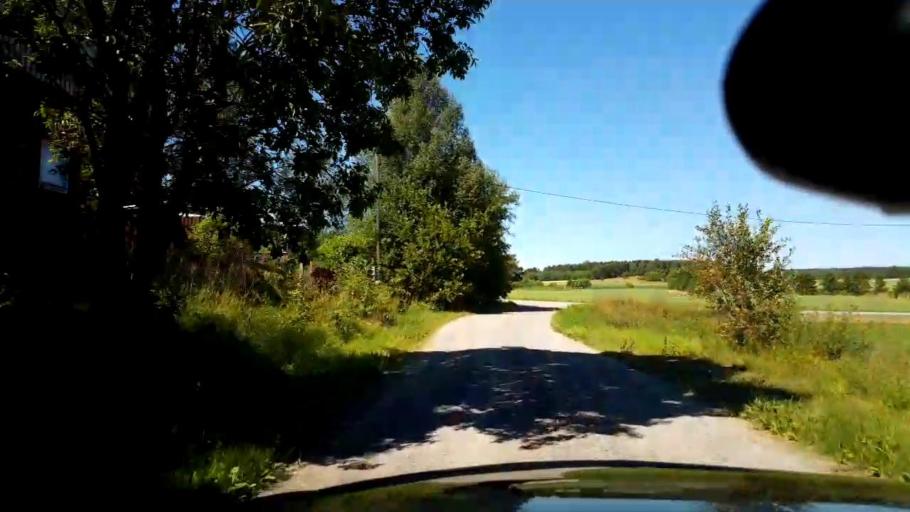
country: SE
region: Uppsala
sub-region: Habo Kommun
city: Balsta
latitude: 59.6188
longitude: 17.6117
